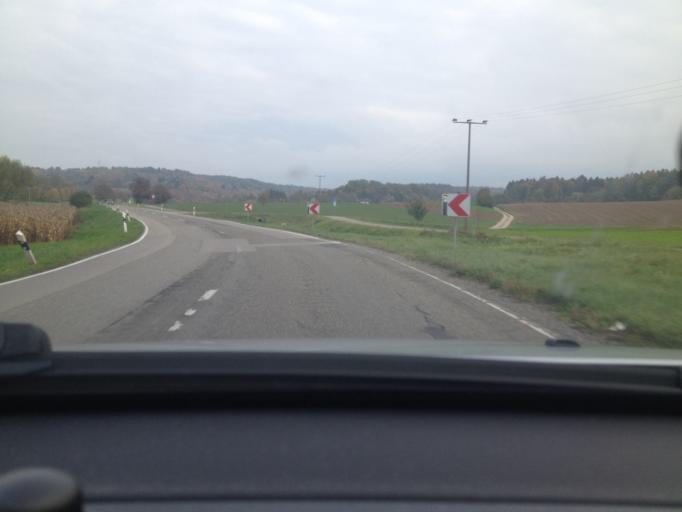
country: DE
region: Baden-Wuerttemberg
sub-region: Karlsruhe Region
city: Konigsbach-Stein
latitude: 48.9387
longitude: 8.5919
